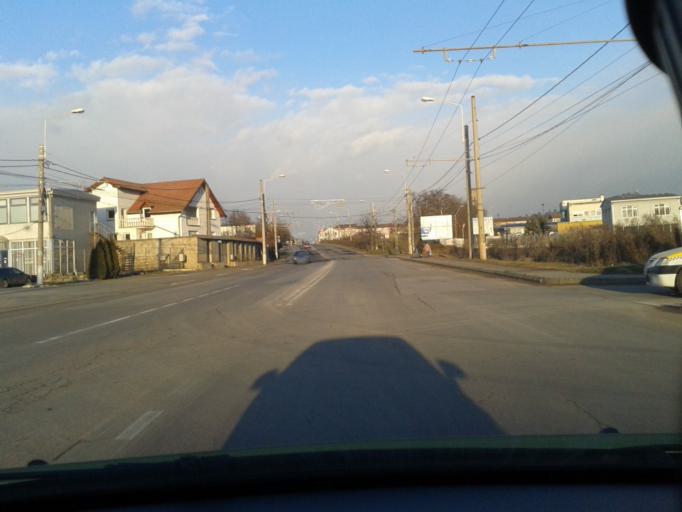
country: RO
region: Sibiu
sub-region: Municipiul Medias
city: Medias
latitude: 46.1456
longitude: 24.3230
